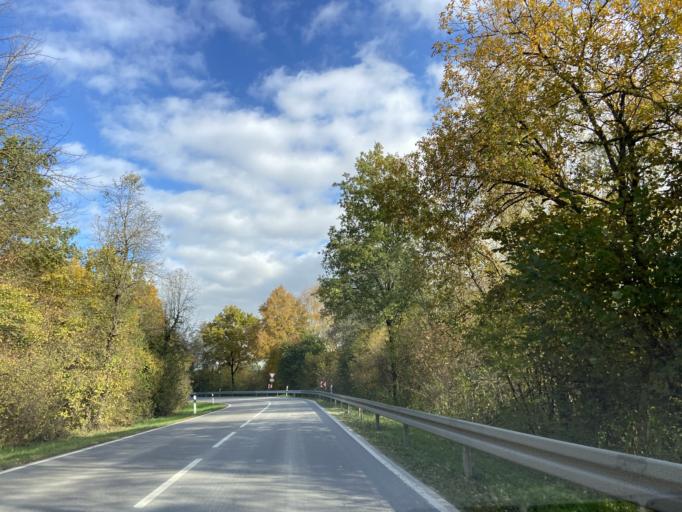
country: DE
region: Baden-Wuerttemberg
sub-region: Tuebingen Region
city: Inzigkofen
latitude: 48.0703
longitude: 9.1886
